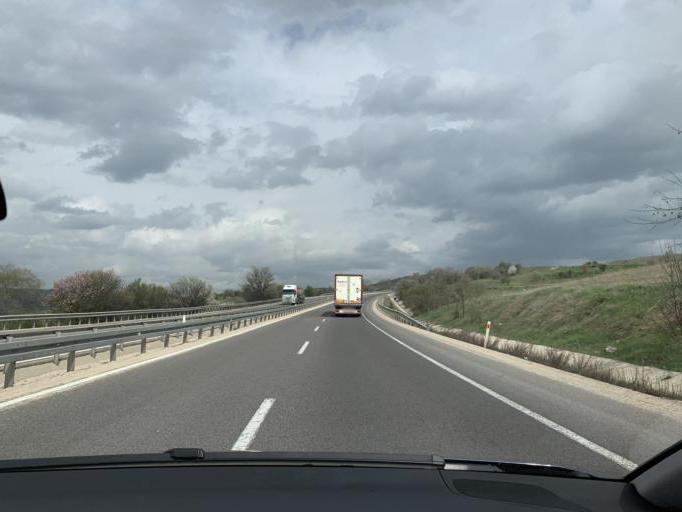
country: TR
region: Bolu
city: Yenicaga
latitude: 40.7827
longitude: 32.0794
